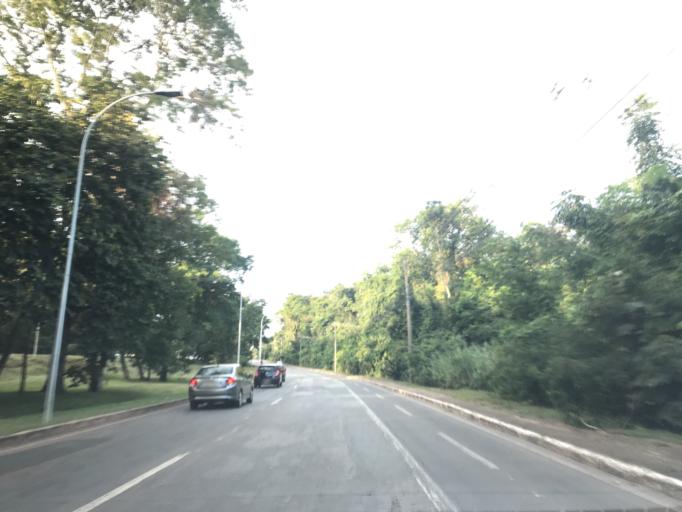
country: BR
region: Federal District
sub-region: Brasilia
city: Brasilia
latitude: -15.8346
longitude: -47.8167
